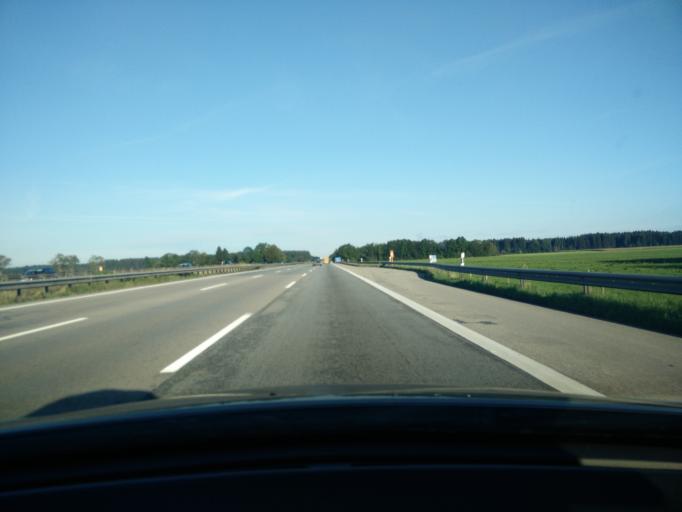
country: DE
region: Bavaria
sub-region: Upper Bavaria
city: Valley
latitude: 47.8800
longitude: 11.7594
